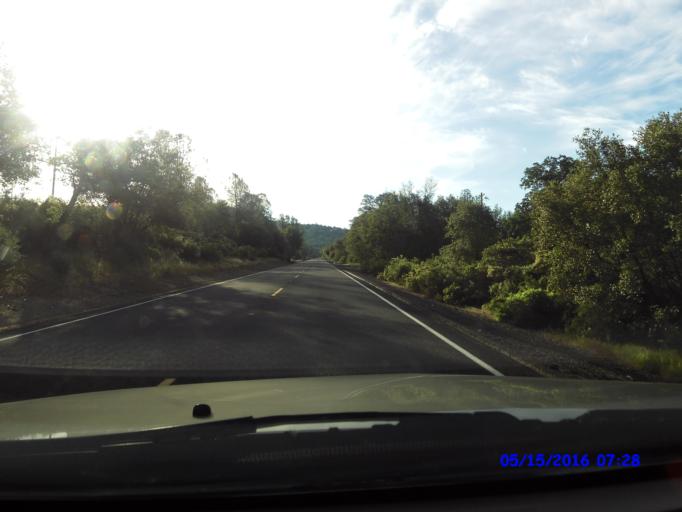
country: US
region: California
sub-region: Tuolumne County
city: Tuolumne City
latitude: 37.7348
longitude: -120.2248
